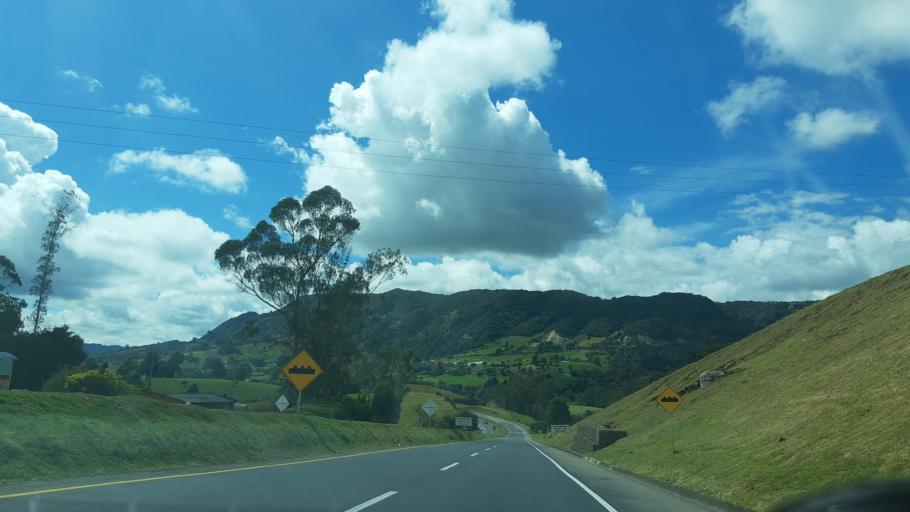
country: CO
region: Boyaca
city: Ventaquemada
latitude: 5.3978
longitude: -73.4884
